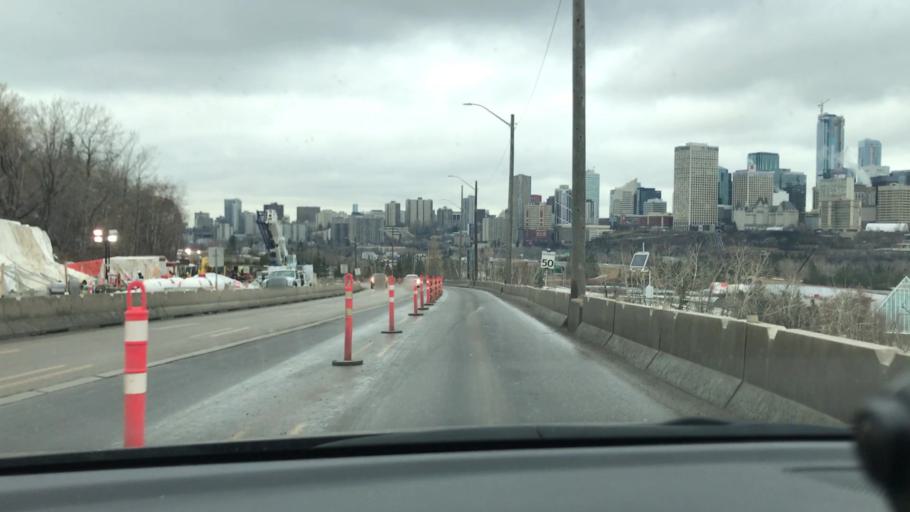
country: CA
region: Alberta
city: Edmonton
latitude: 53.5328
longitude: -113.4741
